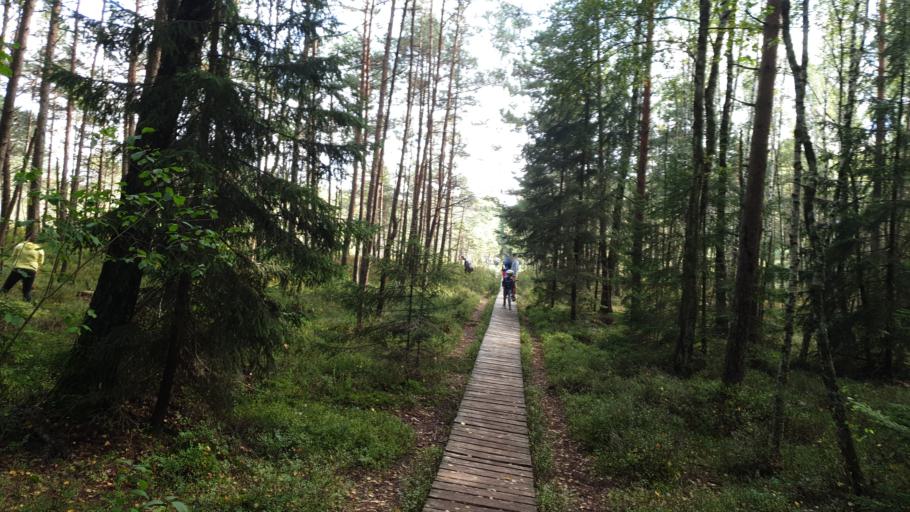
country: LT
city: Trakai
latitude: 54.6430
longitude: 24.9679
